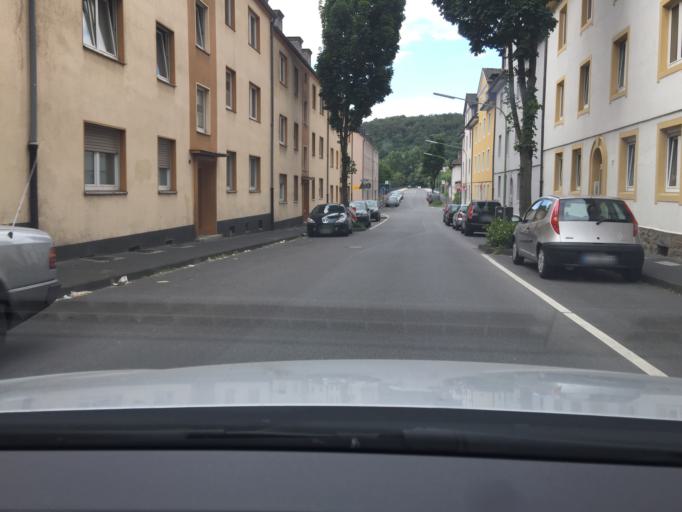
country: DE
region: North Rhine-Westphalia
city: Herdecke
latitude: 51.3838
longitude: 7.4294
